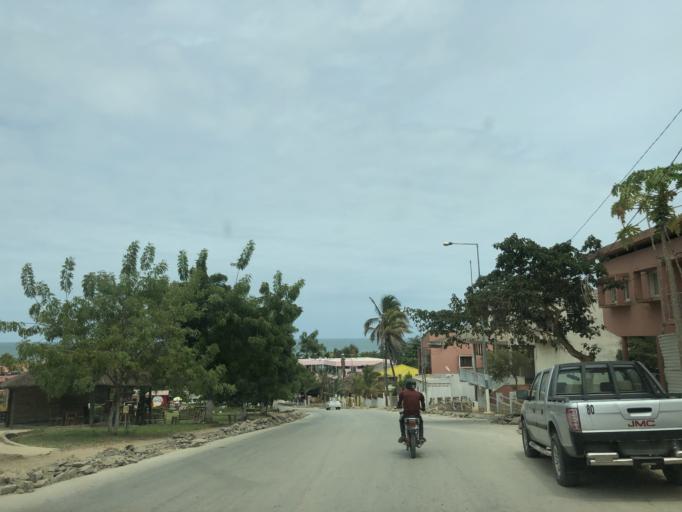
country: AO
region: Cuanza Sul
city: Sumbe
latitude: -11.1960
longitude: 13.8377
